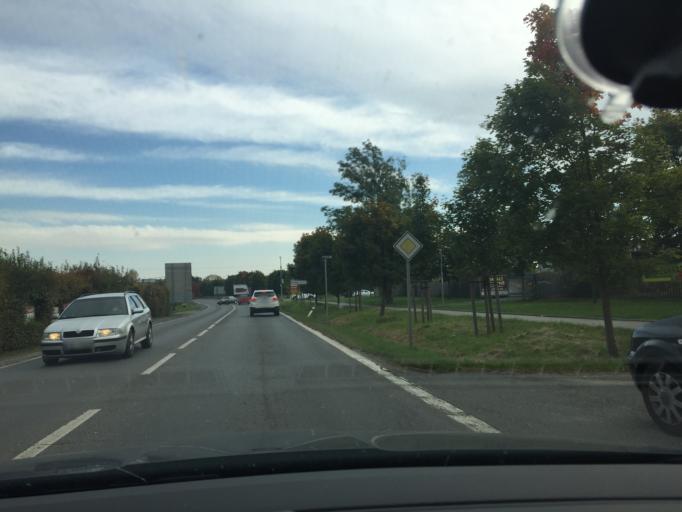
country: CZ
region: Praha
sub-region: Praha 14
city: Dolni Pocernice
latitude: 50.0807
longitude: 14.6028
